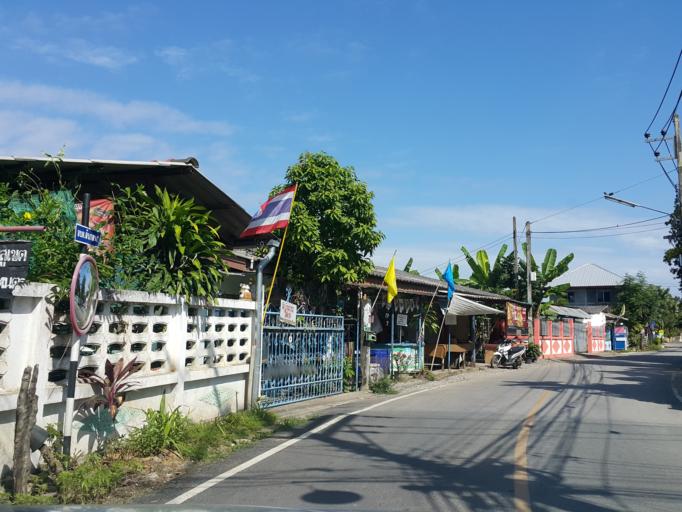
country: TH
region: Chiang Mai
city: San Sai
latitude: 18.7992
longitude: 99.0460
